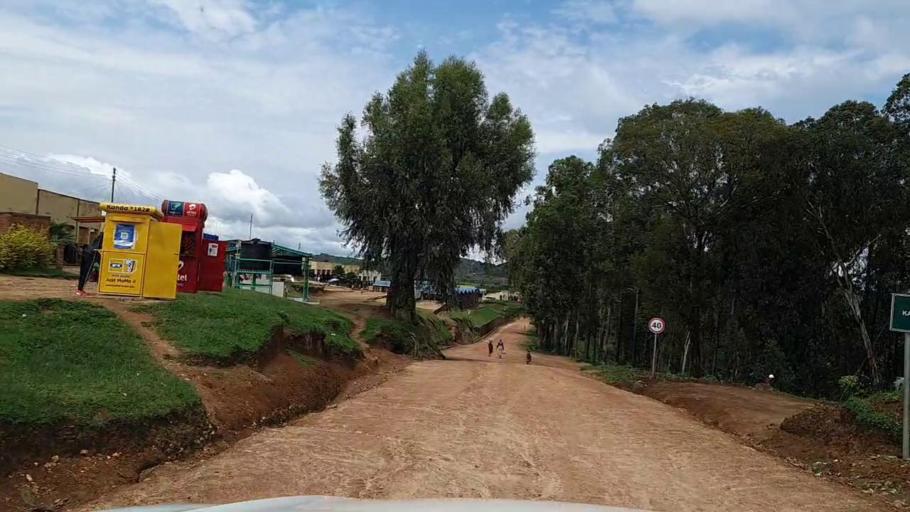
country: RW
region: Southern Province
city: Gikongoro
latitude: -2.3287
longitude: 29.5308
